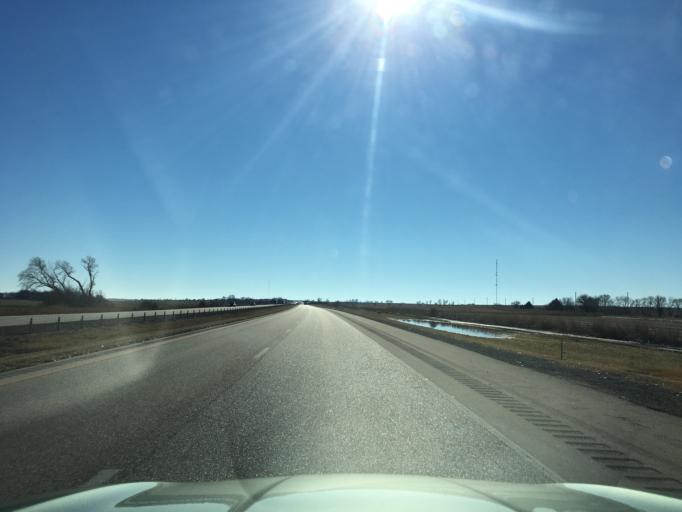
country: US
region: Oklahoma
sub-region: Kay County
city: Blackwell
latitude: 36.8938
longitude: -97.3539
